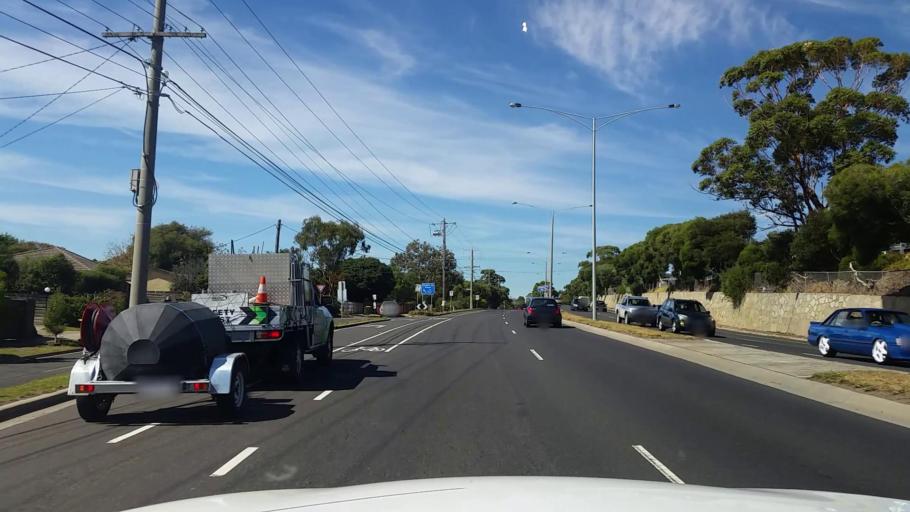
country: AU
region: Victoria
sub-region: Frankston
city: Frankston East
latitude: -38.1484
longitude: 145.1462
